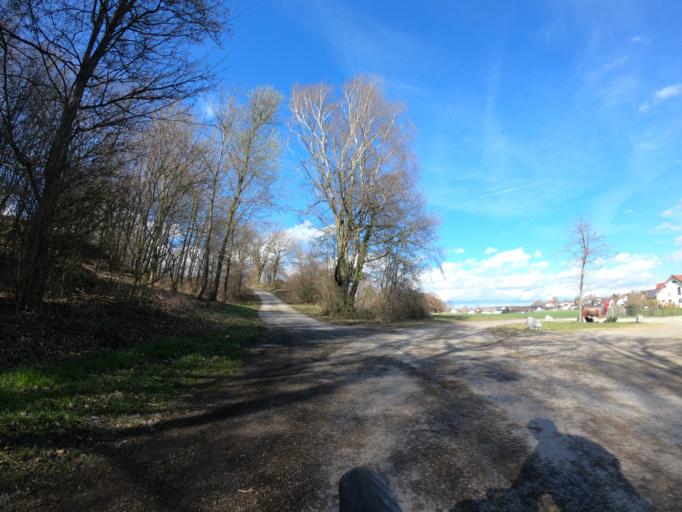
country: DE
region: Bavaria
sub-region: Upper Bavaria
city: Landsberied
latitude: 48.1746
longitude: 11.1818
